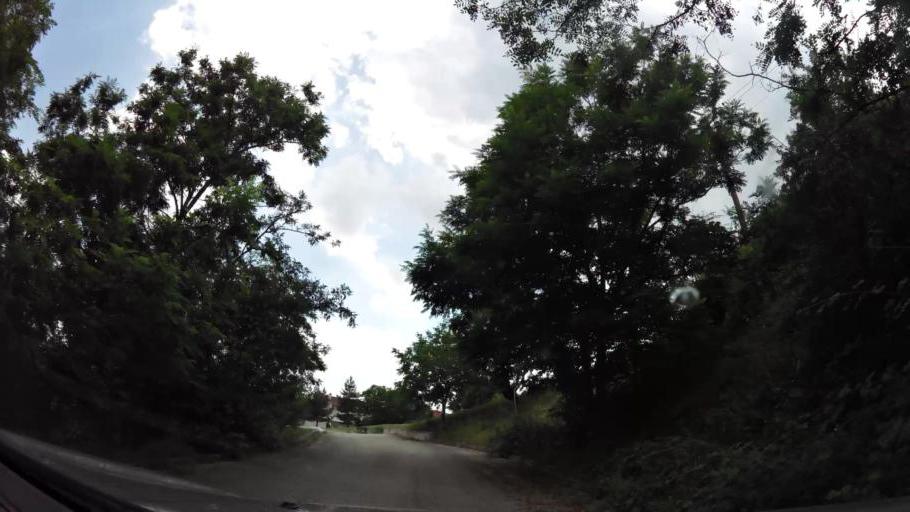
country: GR
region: West Macedonia
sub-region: Nomos Kozanis
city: Koila
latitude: 40.3236
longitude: 21.8244
